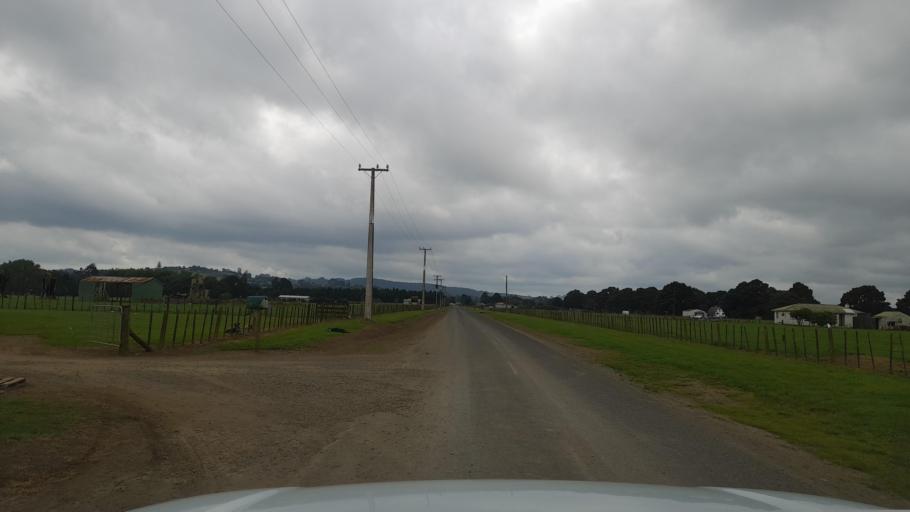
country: NZ
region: Northland
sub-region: Far North District
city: Waimate North
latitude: -35.4311
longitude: 173.7936
